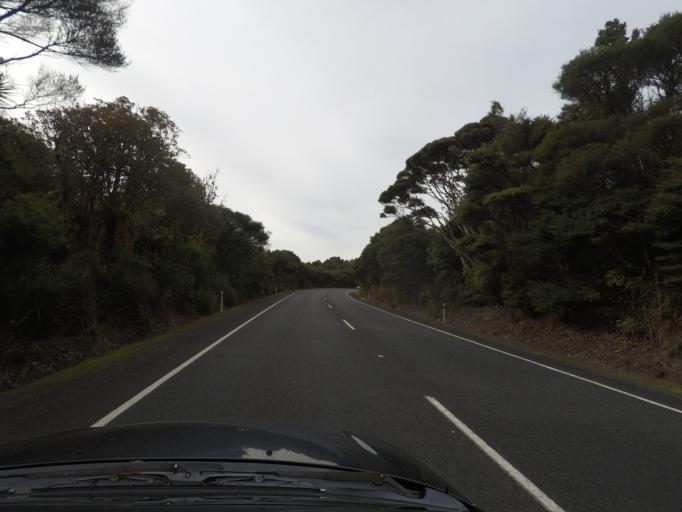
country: NZ
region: Auckland
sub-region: Auckland
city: Titirangi
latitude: -36.9442
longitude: 174.5307
